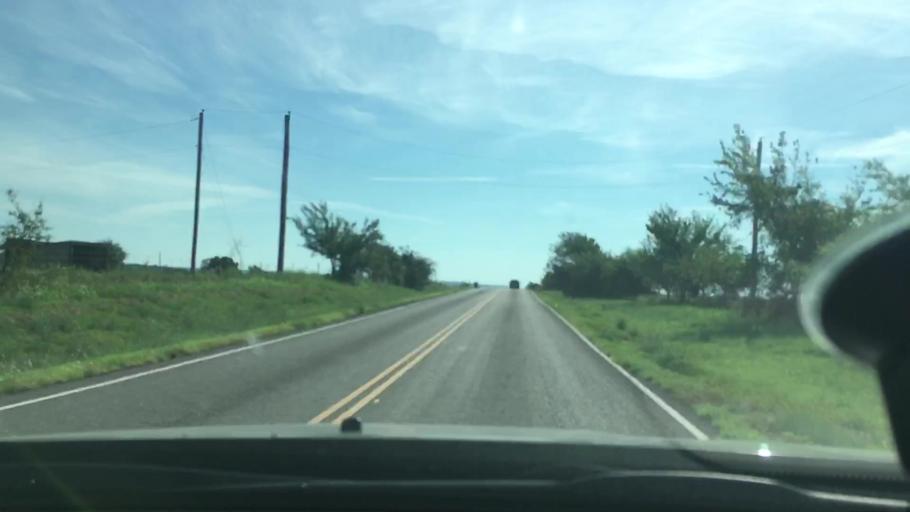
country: US
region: Oklahoma
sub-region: Carter County
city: Lone Grove
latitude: 34.3327
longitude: -97.2185
